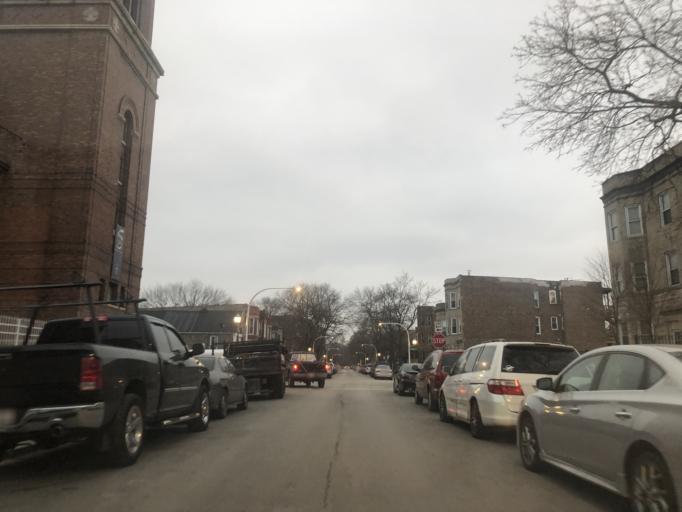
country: US
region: Illinois
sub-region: Cook County
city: Chicago
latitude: 41.7773
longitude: -87.6047
